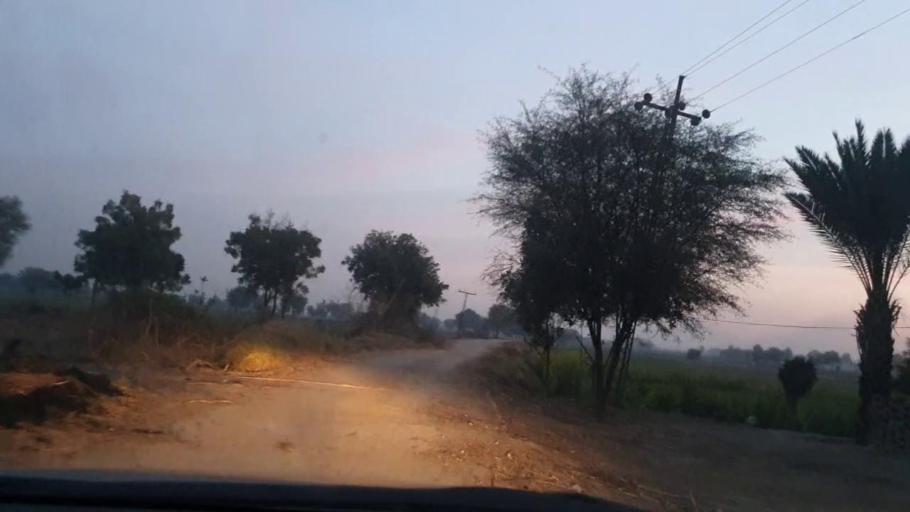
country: PK
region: Sindh
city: Sakrand
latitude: 26.1956
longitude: 68.2974
